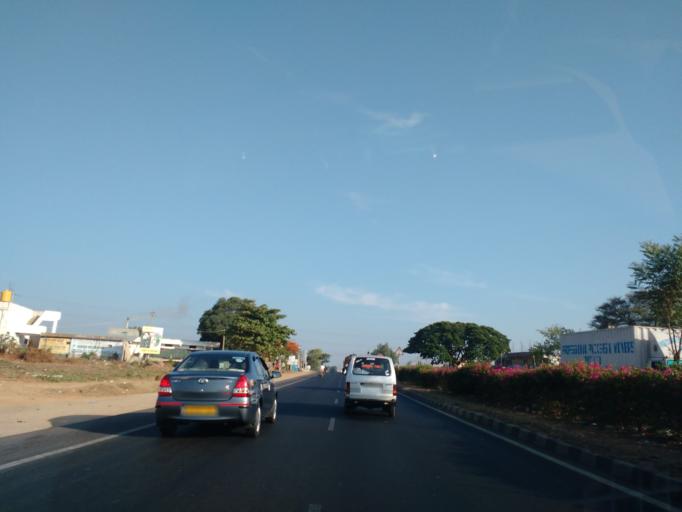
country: IN
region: Karnataka
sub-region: Bangalore Rural
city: Nelamangala
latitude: 13.1303
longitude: 77.3596
